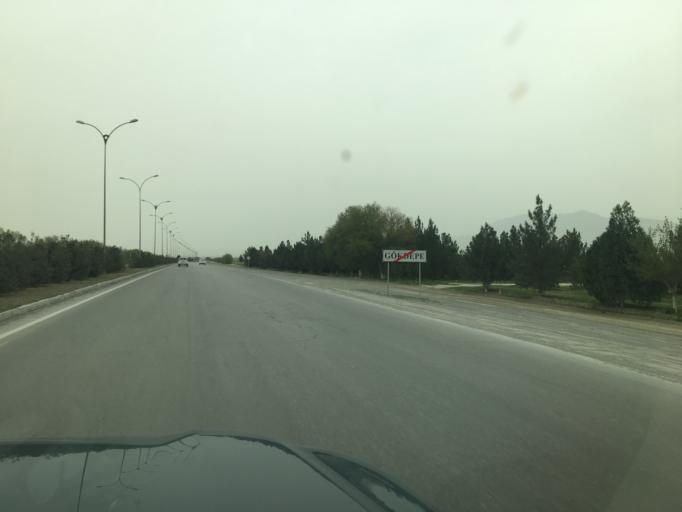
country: TM
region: Ahal
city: Abadan
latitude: 38.1439
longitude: 57.9940
